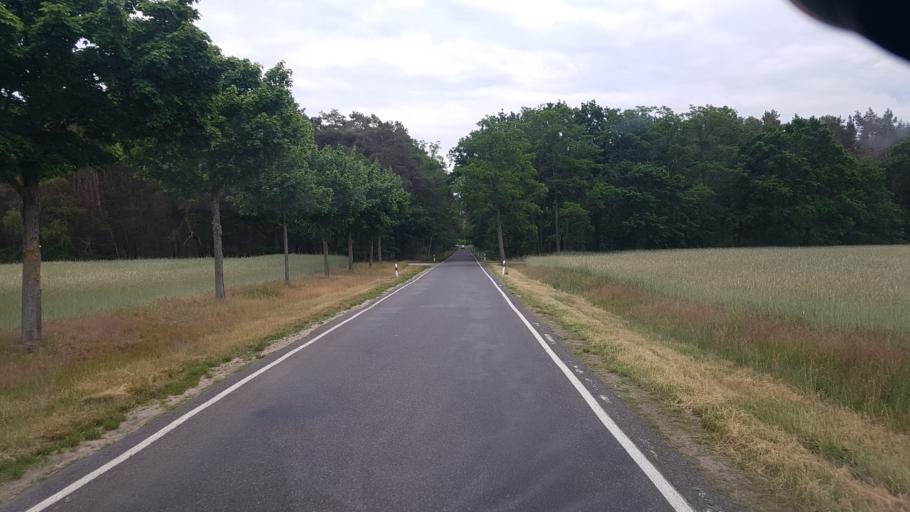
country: DE
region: Brandenburg
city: Herzberg
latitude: 51.7873
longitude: 13.2567
